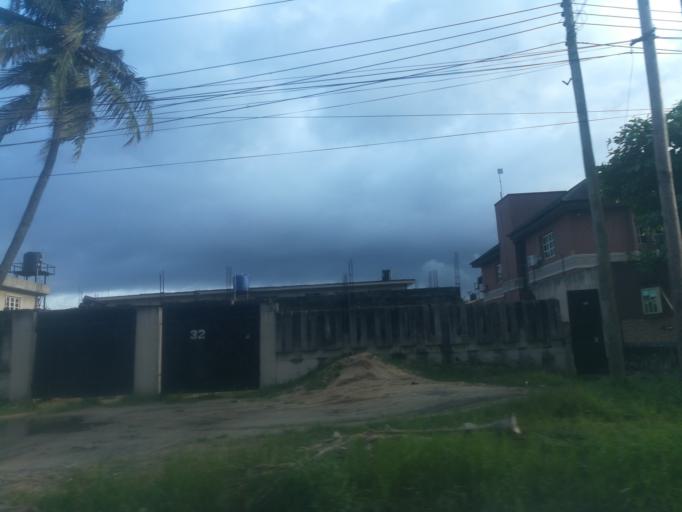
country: NG
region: Lagos
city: Somolu
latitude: 6.5472
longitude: 3.3852
